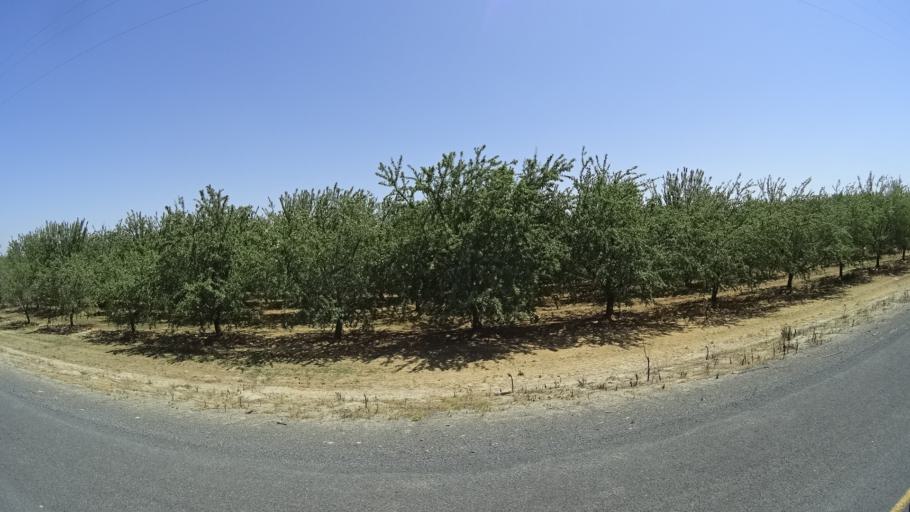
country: US
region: California
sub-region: Kings County
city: Armona
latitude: 36.2602
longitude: -119.7269
